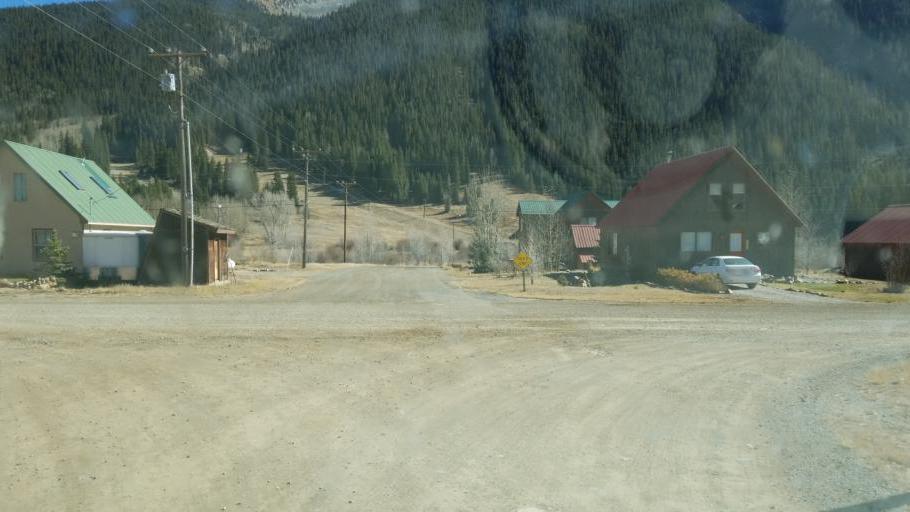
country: US
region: Colorado
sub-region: San Juan County
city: Silverton
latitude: 37.8135
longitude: -107.6588
